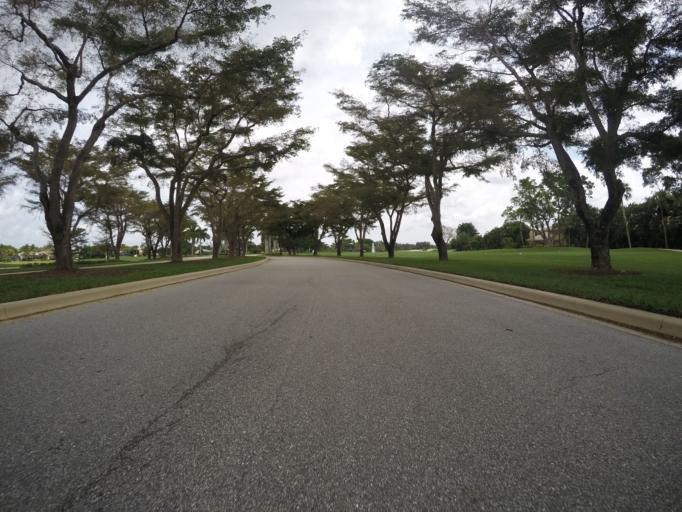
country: US
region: Florida
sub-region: Palm Beach County
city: Villages of Oriole
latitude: 26.4122
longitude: -80.2085
